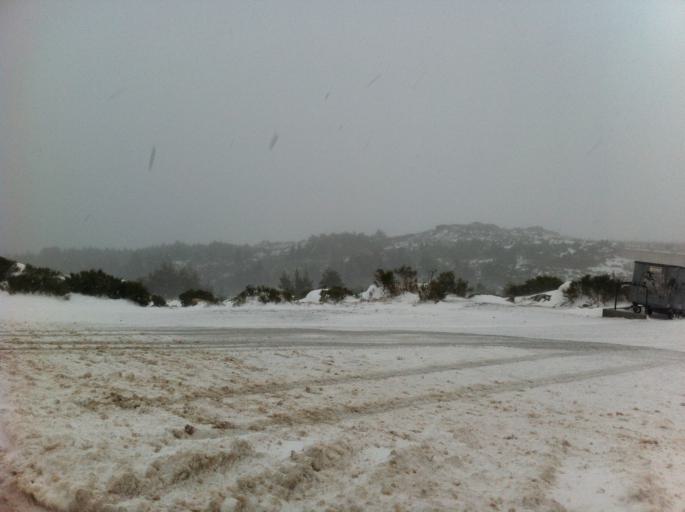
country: PT
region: Castelo Branco
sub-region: Covilha
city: Covilha
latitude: 40.3142
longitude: -7.5602
